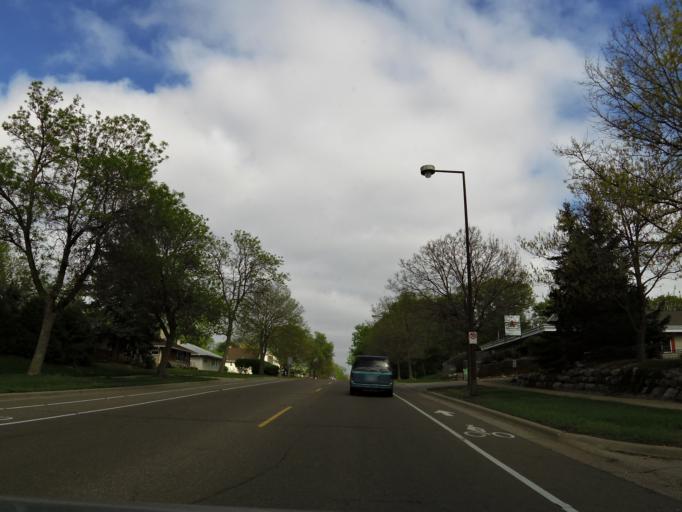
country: US
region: Minnesota
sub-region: Ramsey County
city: Maplewood
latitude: 44.9486
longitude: -93.0139
